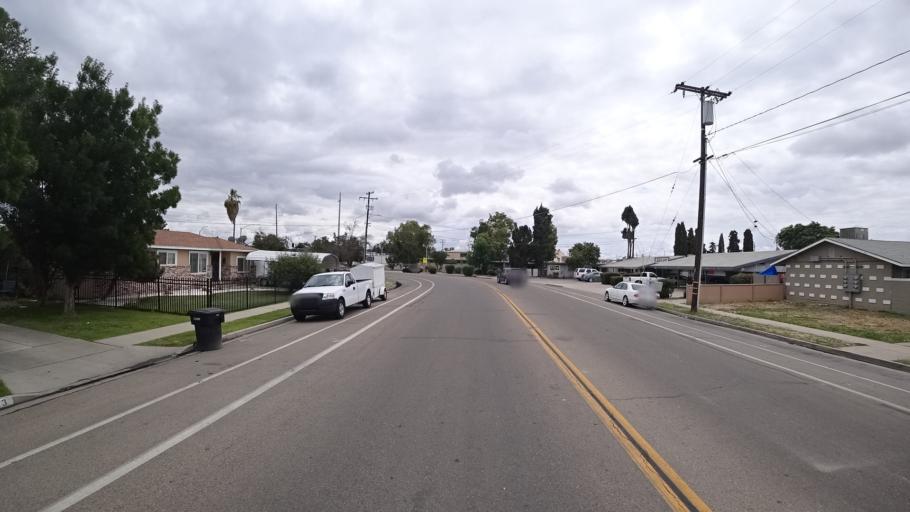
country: US
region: California
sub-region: Kings County
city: Hanford
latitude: 36.3354
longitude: -119.6562
